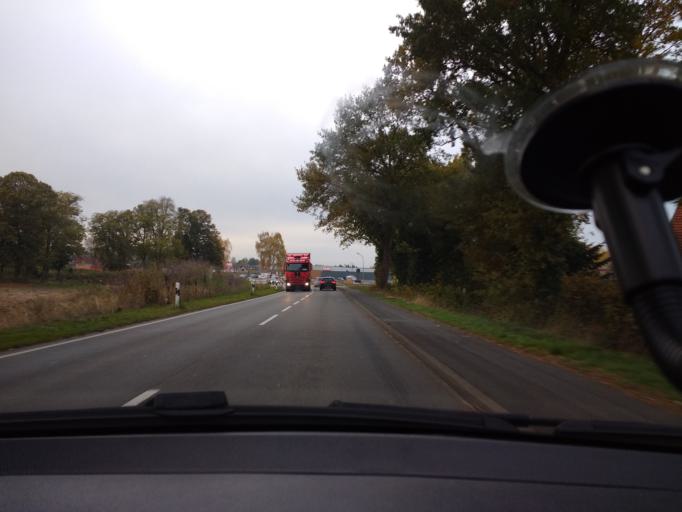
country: DE
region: Lower Saxony
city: Calberlah
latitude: 52.4186
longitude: 10.6354
